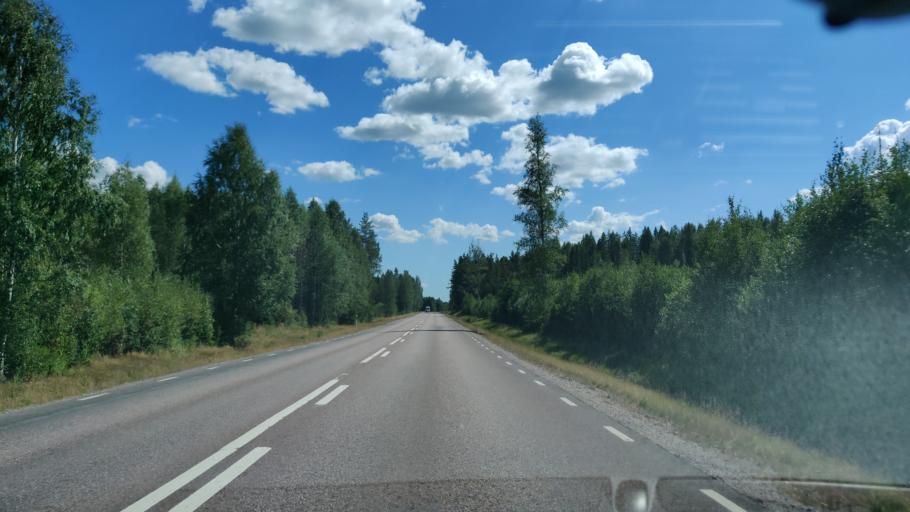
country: SE
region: Vaermland
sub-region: Hagfors Kommun
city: Ekshaerad
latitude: 60.2104
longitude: 13.4860
